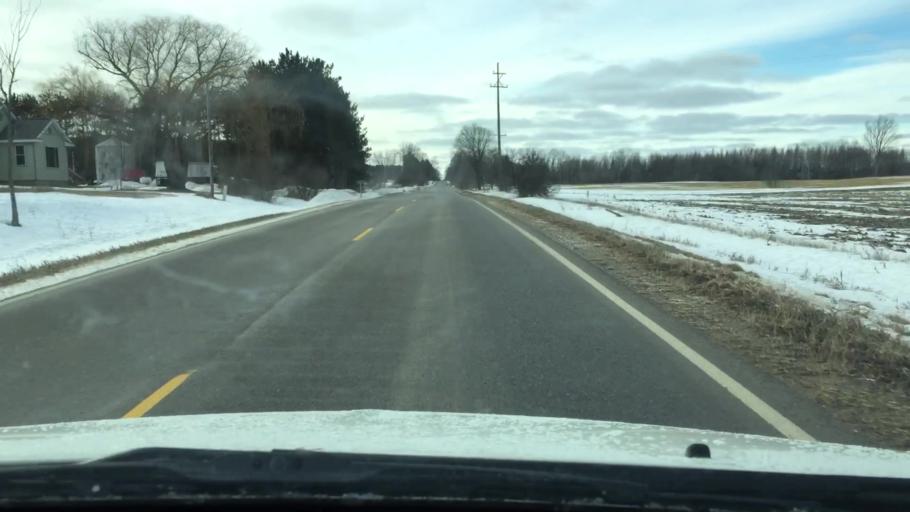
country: US
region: Michigan
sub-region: Wexford County
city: Manton
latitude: 44.4036
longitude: -85.4215
